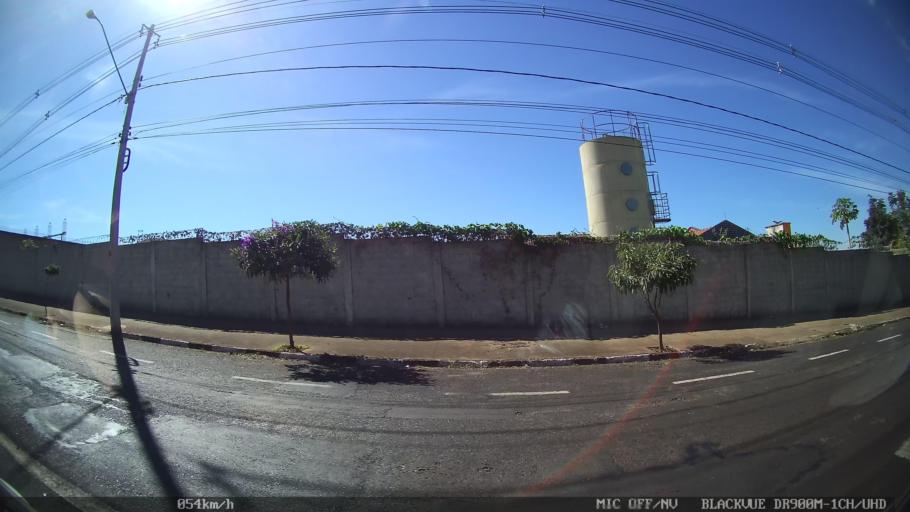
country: BR
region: Sao Paulo
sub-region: Franca
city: Franca
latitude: -20.5470
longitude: -47.3736
